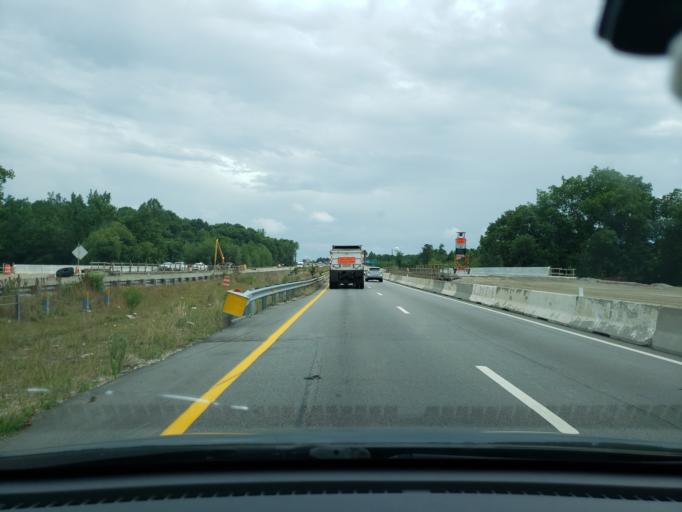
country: US
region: North Carolina
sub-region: Wake County
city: Garner
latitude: 35.6229
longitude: -78.5671
